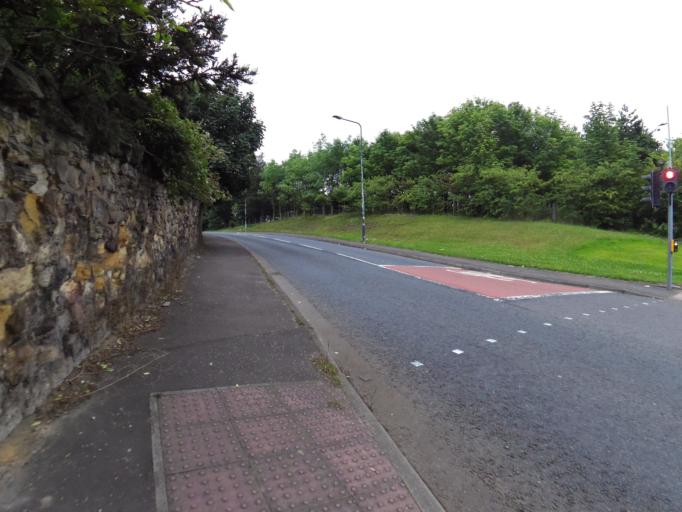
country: GB
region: Scotland
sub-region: Midlothian
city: Bonnyrigg
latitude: 55.9135
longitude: -3.1177
